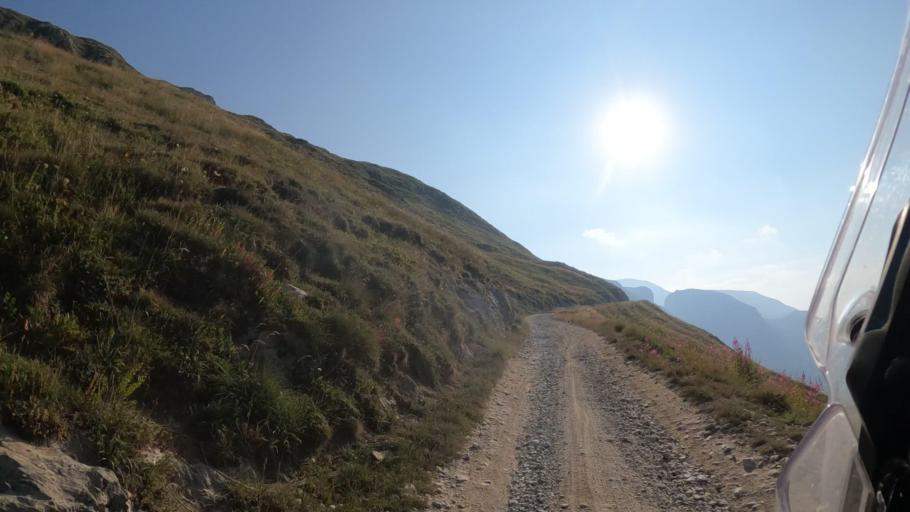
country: IT
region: Piedmont
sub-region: Provincia di Cuneo
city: Limone Piemonte
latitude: 44.1651
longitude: 7.6331
